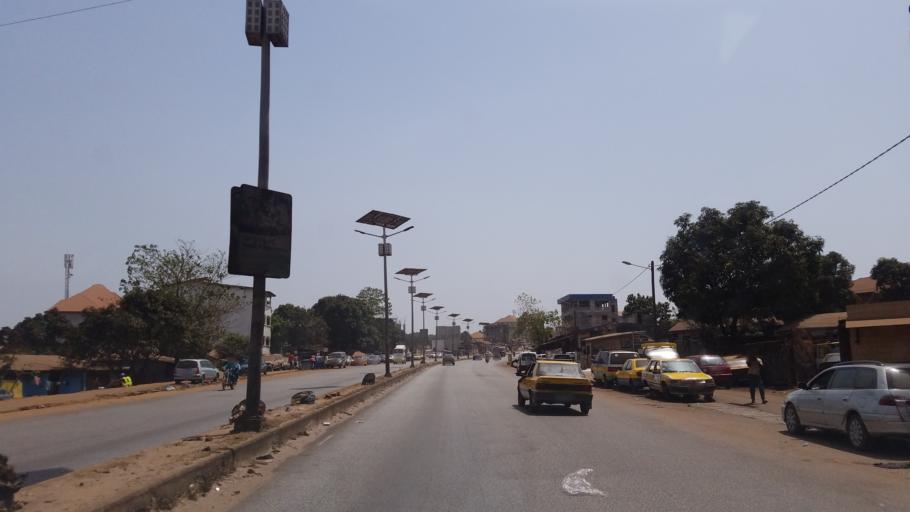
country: GN
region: Conakry
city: Conakry
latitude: 9.6463
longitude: -13.5855
